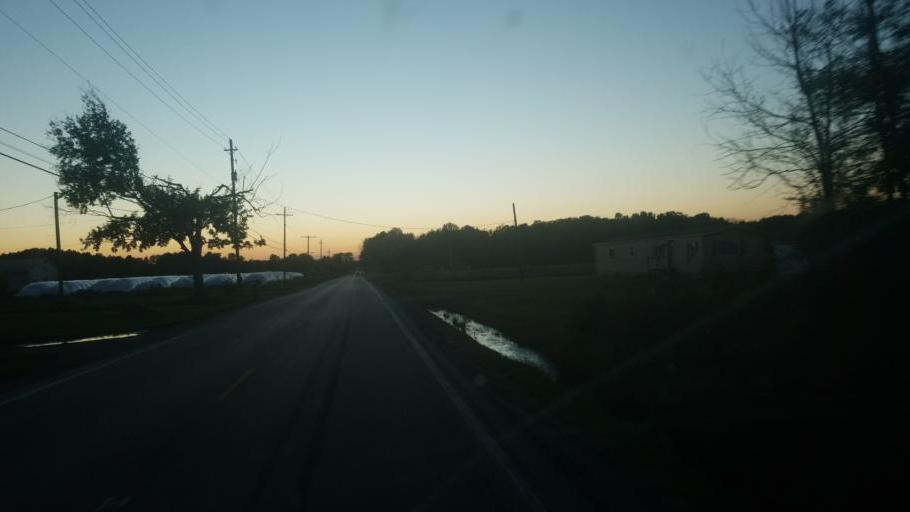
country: US
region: Ohio
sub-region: Ashtabula County
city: Andover
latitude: 41.7514
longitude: -80.5924
